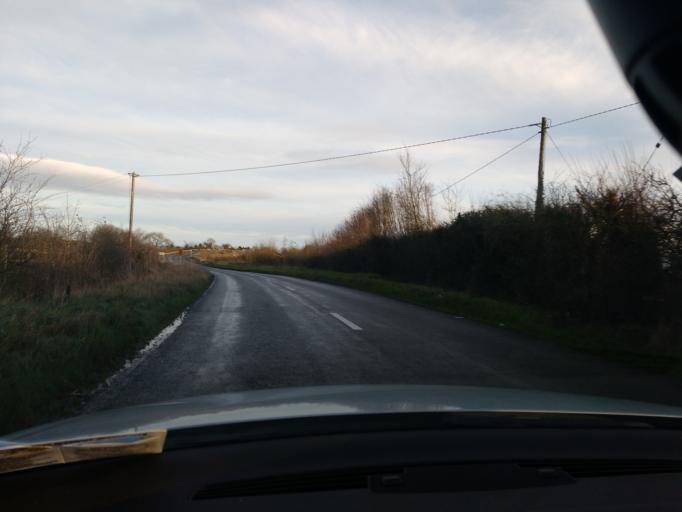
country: IE
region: Munster
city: Thurles
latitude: 52.6322
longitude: -7.7701
